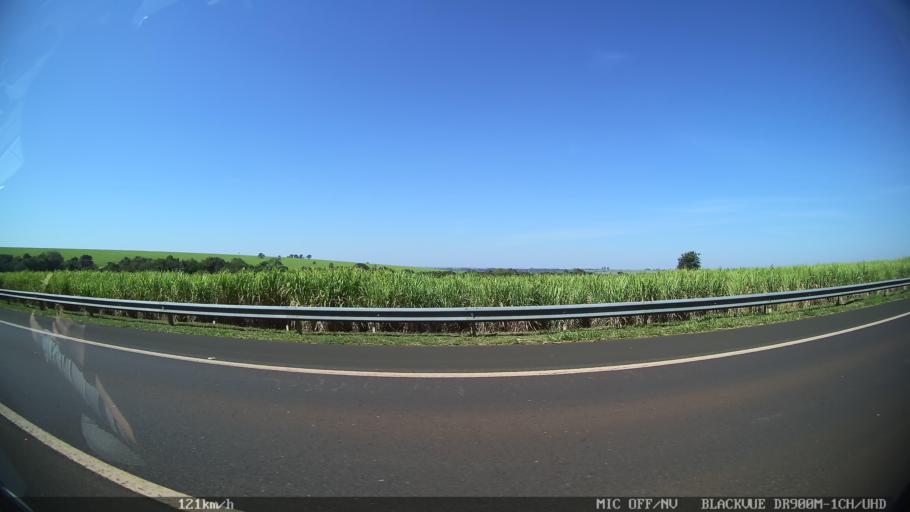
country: BR
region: Sao Paulo
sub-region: Batatais
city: Batatais
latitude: -20.8248
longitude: -47.5929
